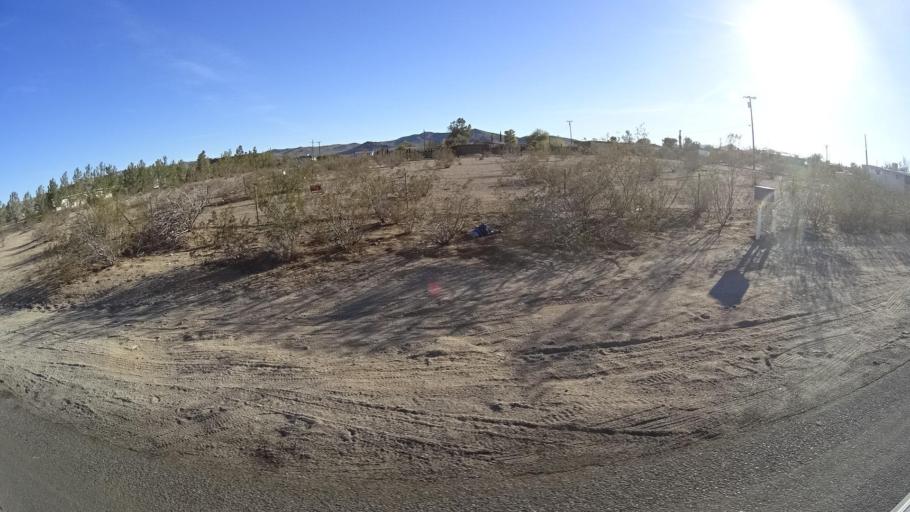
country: US
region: California
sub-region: Kern County
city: Ridgecrest
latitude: 35.6007
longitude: -117.7005
